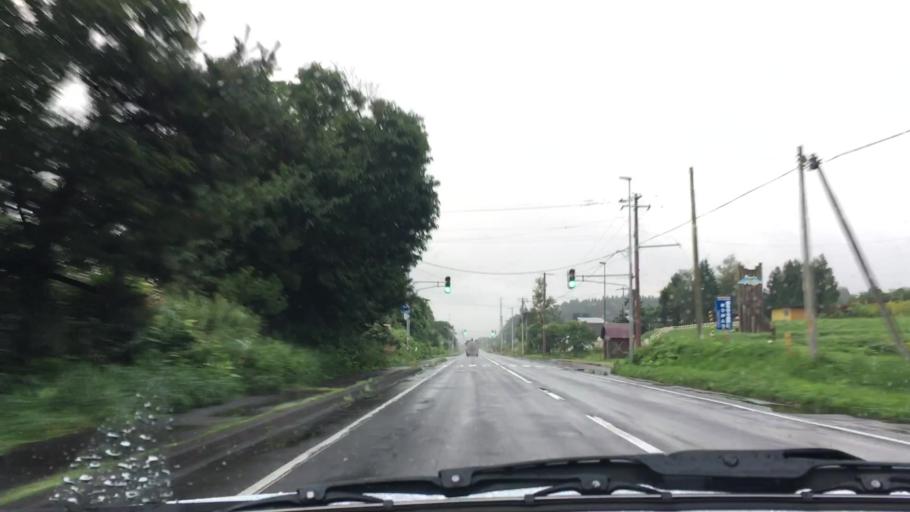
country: JP
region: Hokkaido
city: Nanae
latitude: 42.1756
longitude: 140.4524
